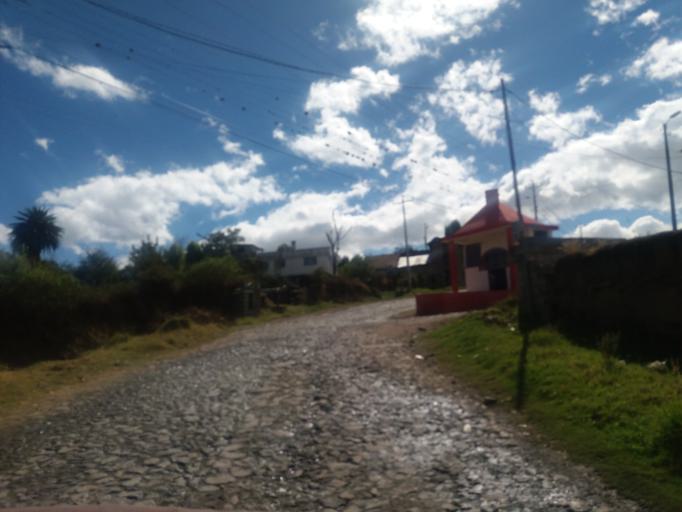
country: EC
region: Pichincha
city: Quito
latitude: -0.1687
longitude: -78.3331
